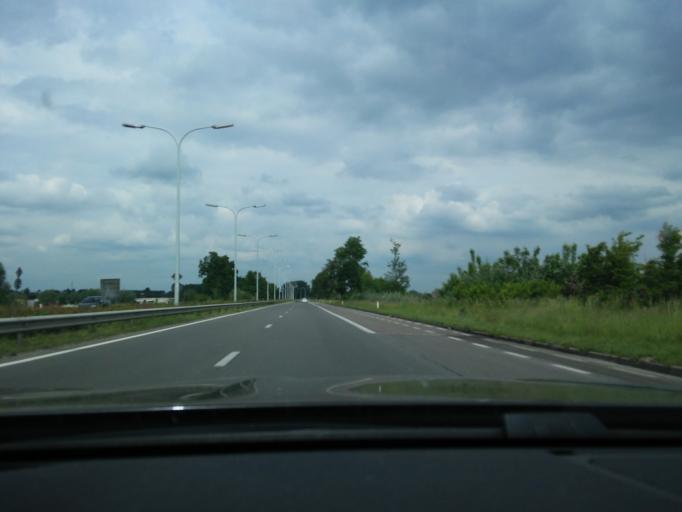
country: BE
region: Flanders
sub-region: Provincie Oost-Vlaanderen
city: Ninove
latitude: 50.8298
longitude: 4.0358
